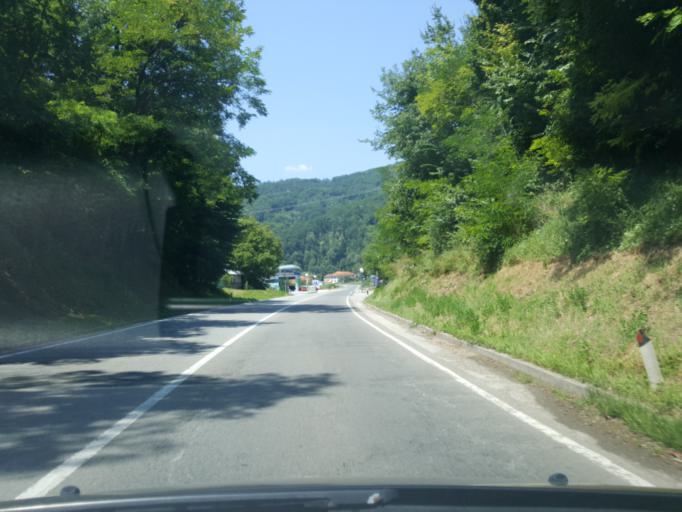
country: RS
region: Central Serbia
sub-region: Moravicki Okrug
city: Gornji Milanovac
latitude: 44.0010
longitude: 20.4404
